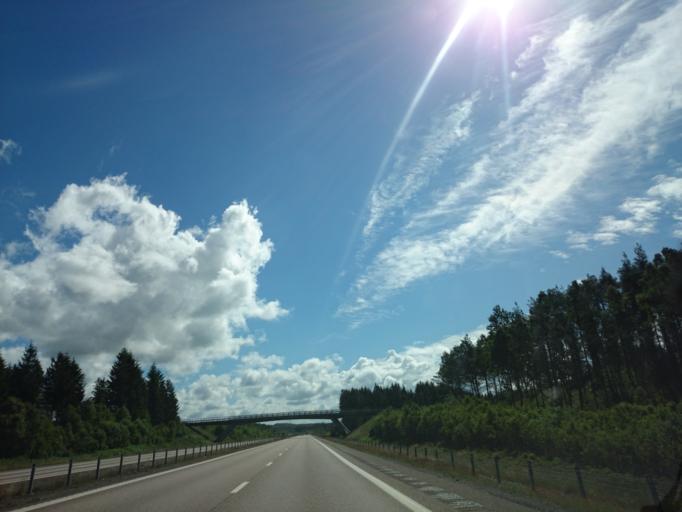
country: SE
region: Skane
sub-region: Orkelljunga Kommun
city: OErkelljunga
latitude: 56.2587
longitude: 13.2534
